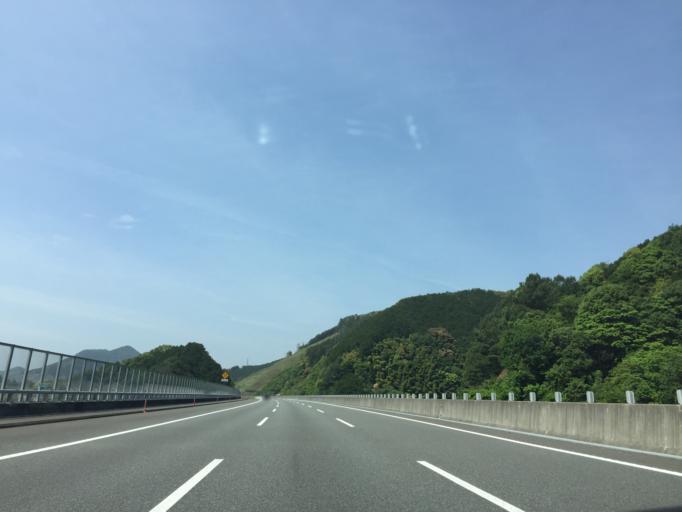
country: JP
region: Shizuoka
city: Shizuoka-shi
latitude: 35.0375
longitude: 138.3683
